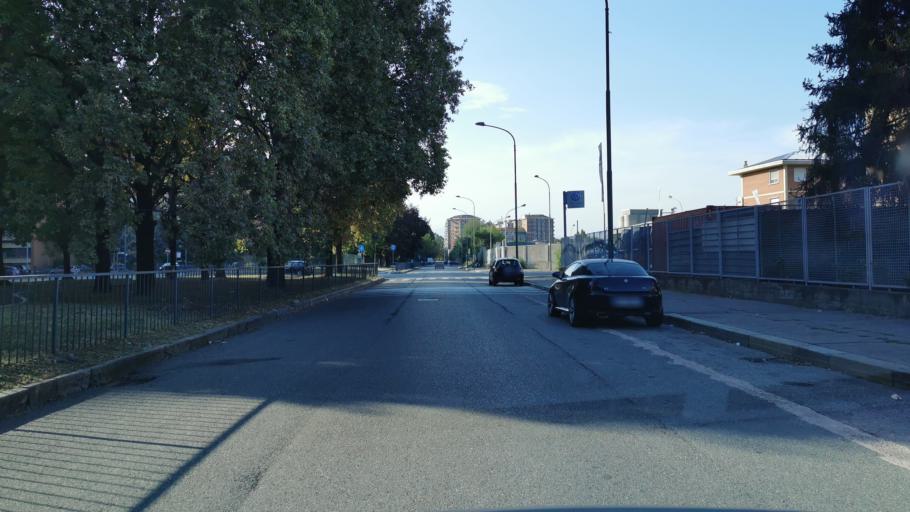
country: IT
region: Piedmont
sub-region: Provincia di Torino
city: Turin
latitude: 45.0981
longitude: 7.7077
